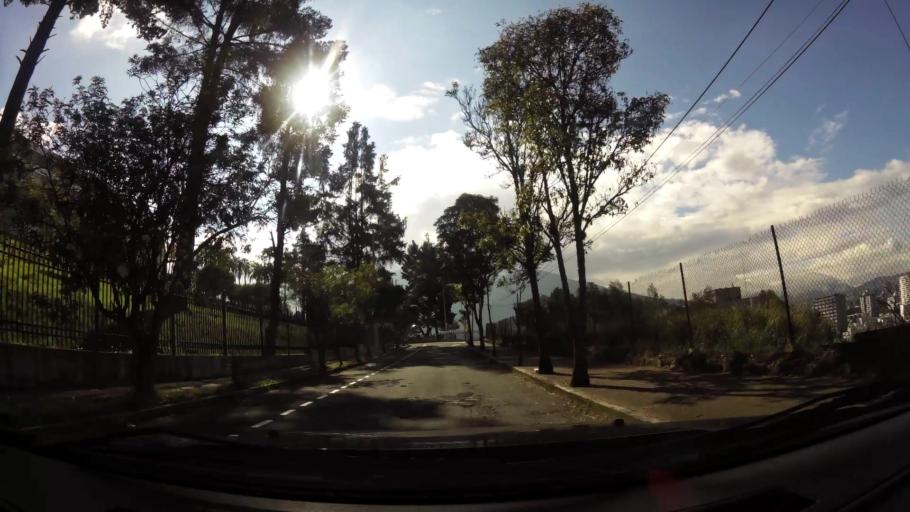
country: EC
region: Pichincha
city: Quito
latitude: -0.2148
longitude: -78.4928
